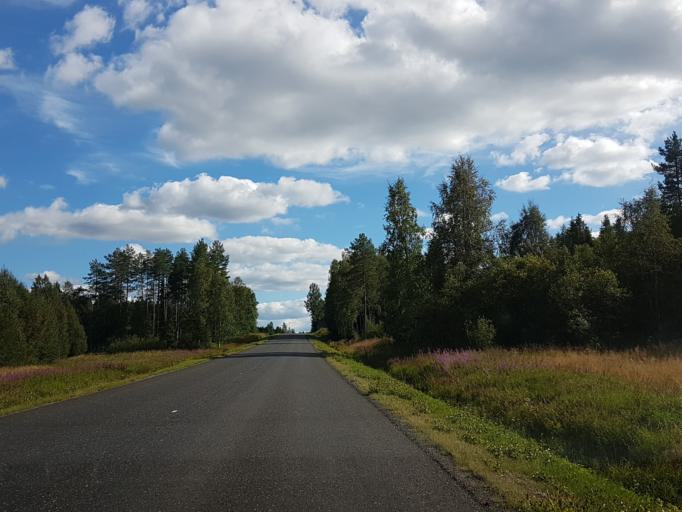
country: SE
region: Vaesterbotten
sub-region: Skelleftea Kommun
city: Burtraesk
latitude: 64.2902
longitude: 20.5243
